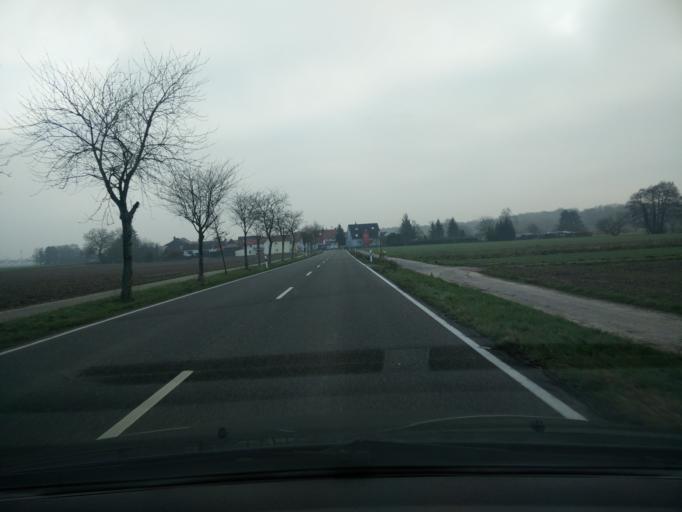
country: DE
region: Rheinland-Pfalz
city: Minfeld
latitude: 49.0732
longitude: 8.1627
